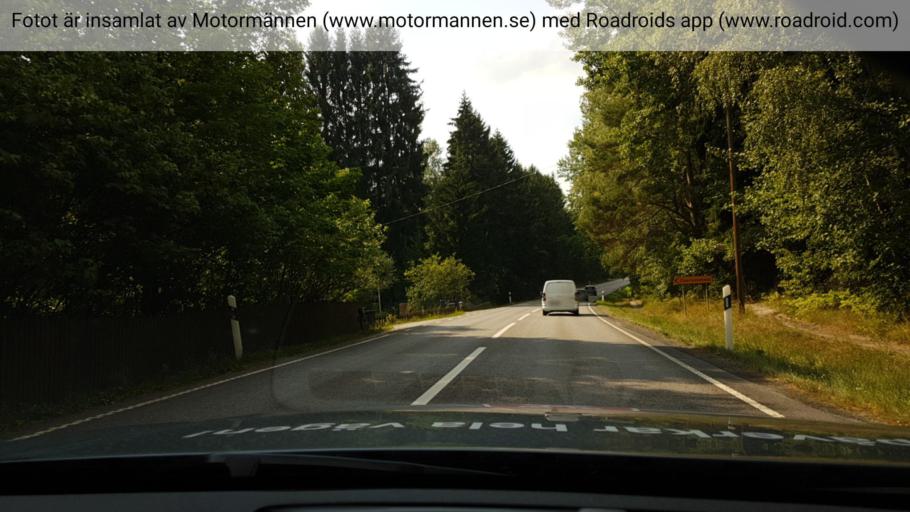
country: SE
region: Soedermanland
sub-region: Gnesta Kommun
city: Gnesta
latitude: 59.0337
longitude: 17.3397
